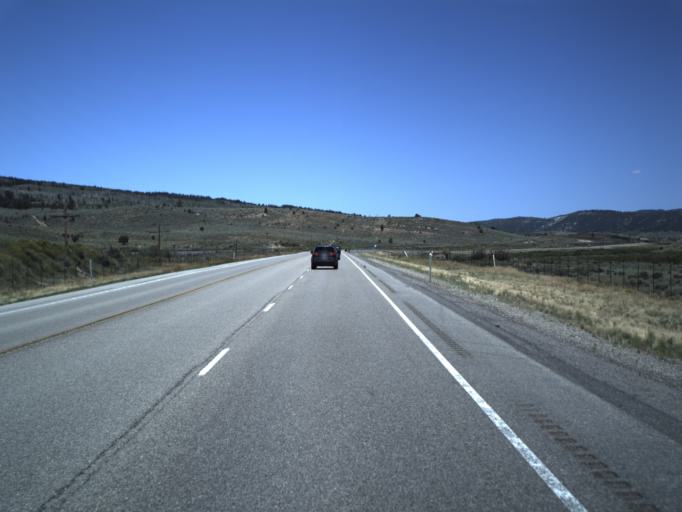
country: US
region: Utah
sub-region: Carbon County
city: Helper
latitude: 39.8811
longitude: -111.0441
